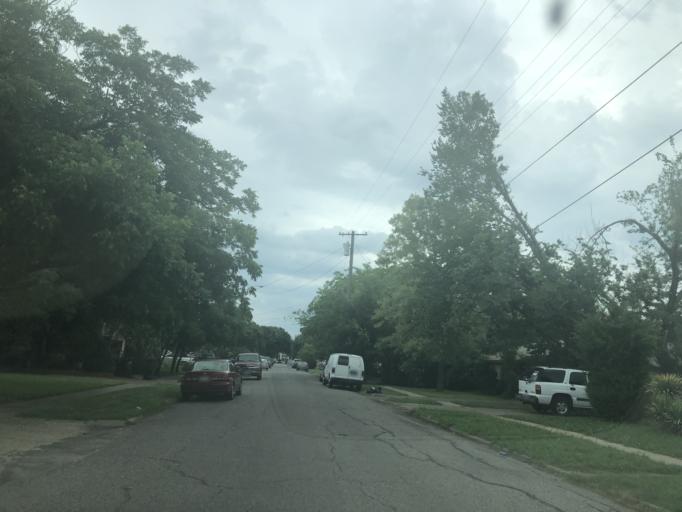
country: US
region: Texas
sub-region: Dallas County
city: Irving
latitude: 32.8096
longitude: -96.9379
